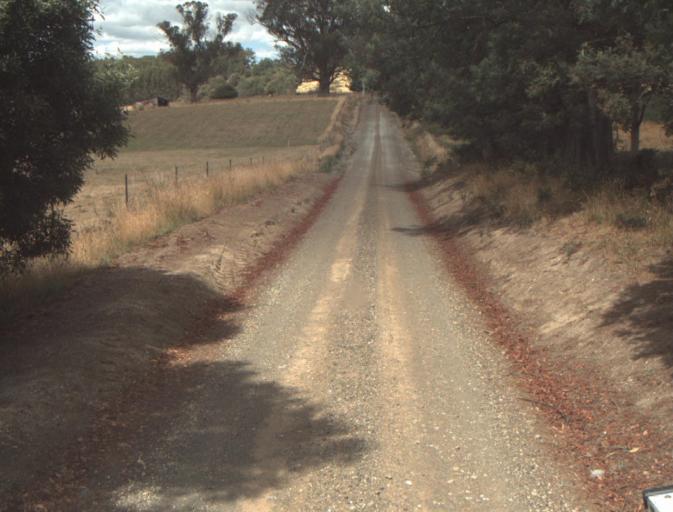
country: AU
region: Tasmania
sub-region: Launceston
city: Mayfield
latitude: -41.1965
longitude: 147.1698
